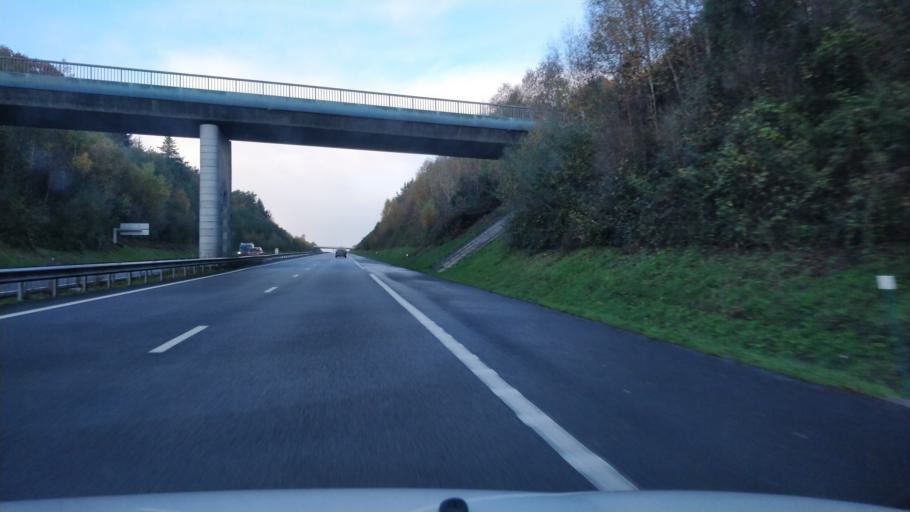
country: FR
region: Brittany
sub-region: Departement du Morbihan
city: Saint-Gonnery
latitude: 48.1303
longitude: -2.8176
